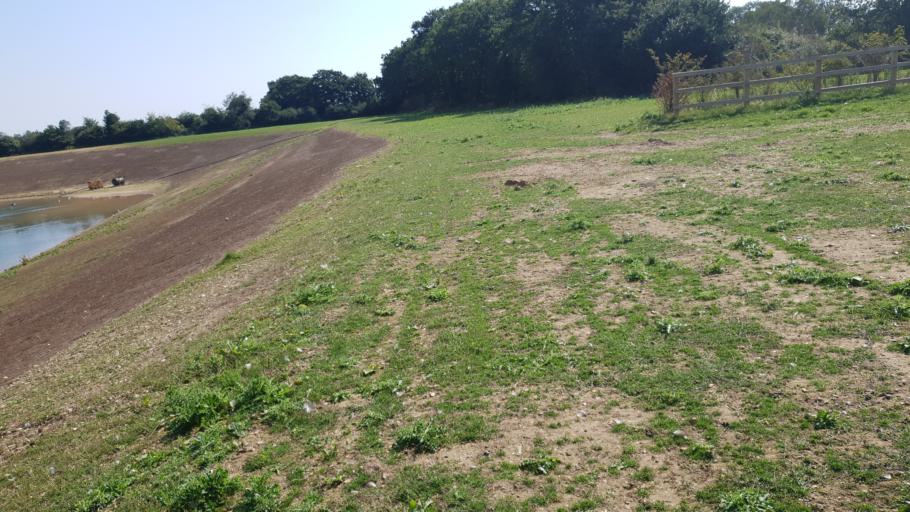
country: GB
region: England
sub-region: Essex
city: Colchester
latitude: 51.9219
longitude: 0.9546
